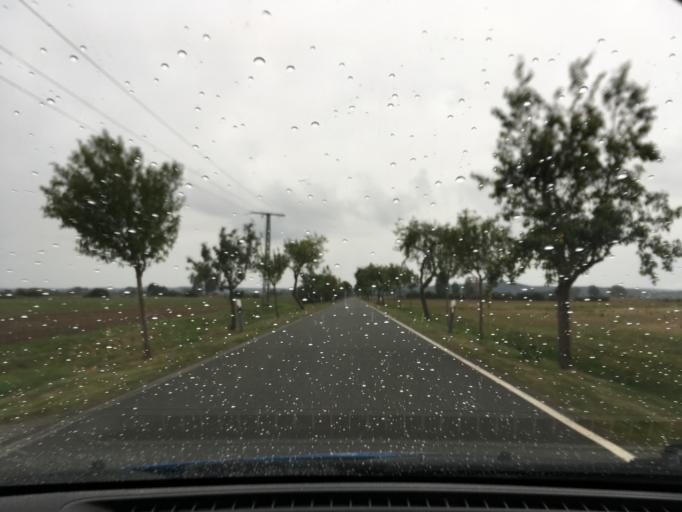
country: DE
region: Lower Saxony
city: Hitzacker
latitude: 53.2219
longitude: 10.9877
